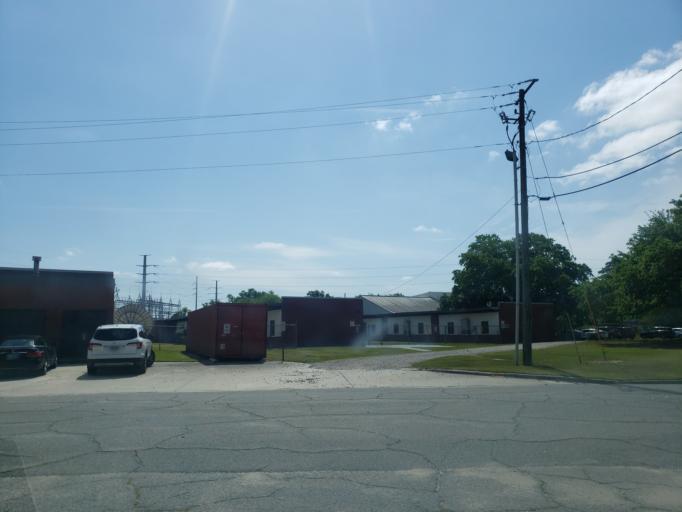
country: US
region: Georgia
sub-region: Chatham County
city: Thunderbolt
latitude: 32.0670
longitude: -81.0513
